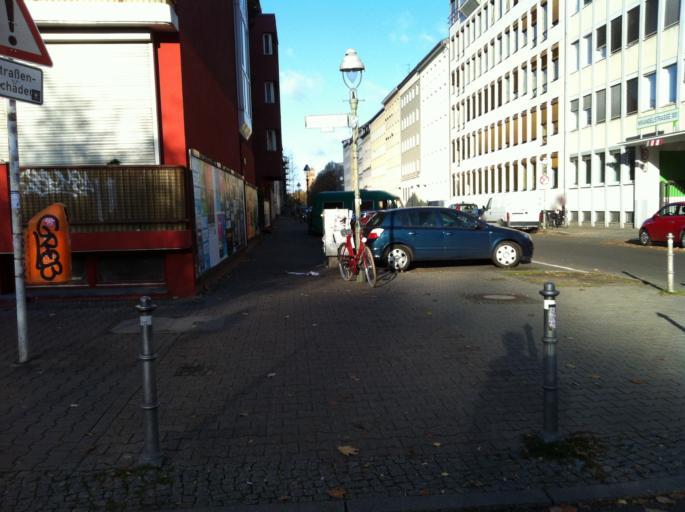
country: DE
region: Berlin
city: Berlin Treptow
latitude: 52.5014
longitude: 13.4350
